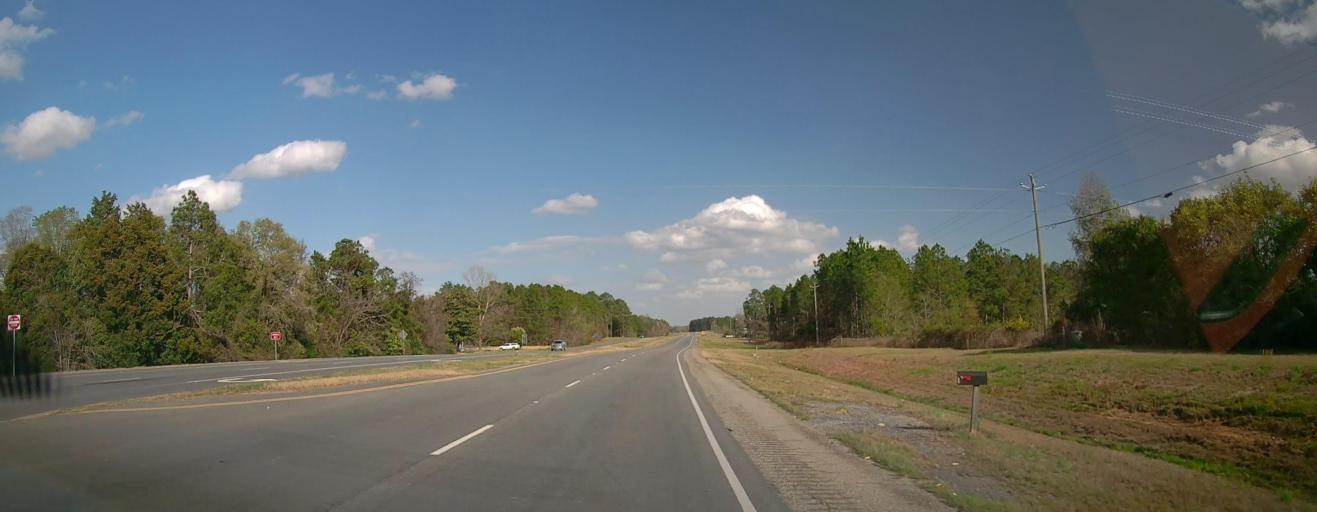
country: US
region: Georgia
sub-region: Telfair County
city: Helena
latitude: 32.1038
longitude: -83.0070
